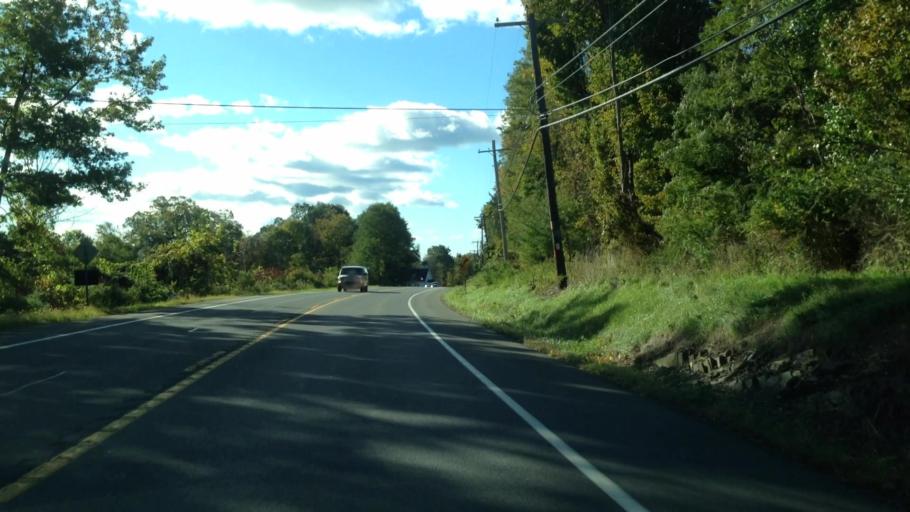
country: US
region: New York
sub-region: Dutchess County
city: Hyde Park
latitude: 41.8357
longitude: -73.9650
